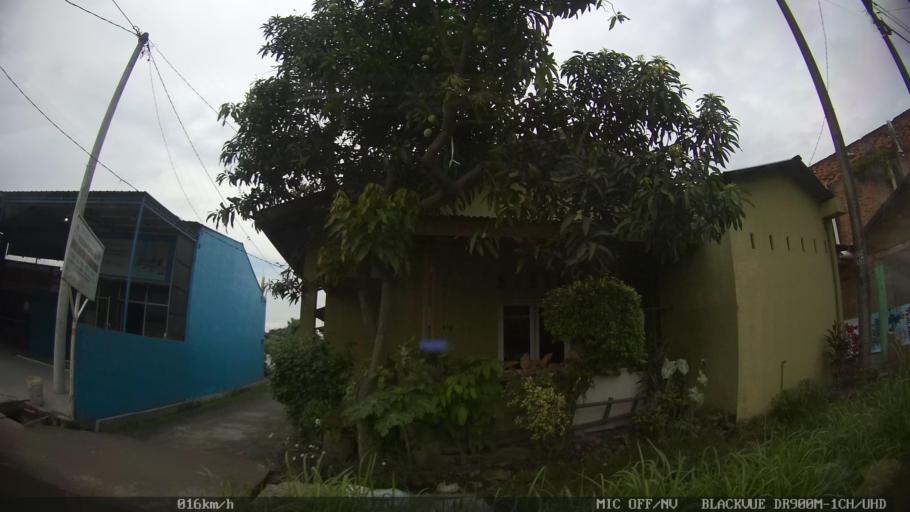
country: ID
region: North Sumatra
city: Sunggal
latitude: 3.6205
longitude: 98.5968
